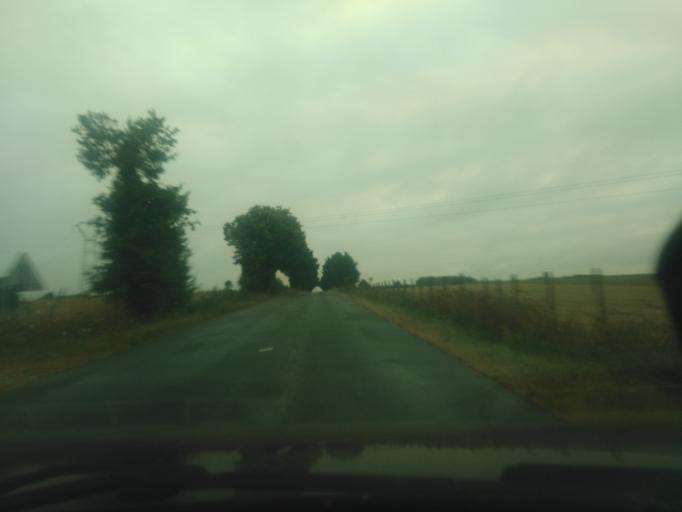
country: FR
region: Pays de la Loire
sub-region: Departement de la Vendee
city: La Ferriere
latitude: 46.7467
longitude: -1.3091
